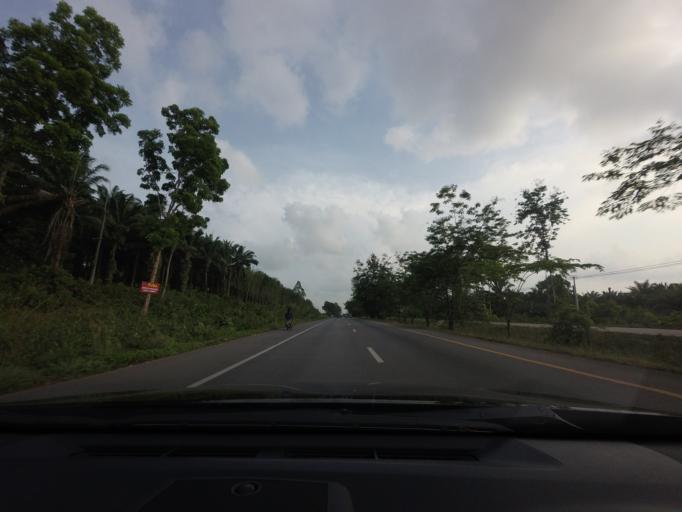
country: TH
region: Chumphon
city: Lang Suan
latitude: 9.8910
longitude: 99.0636
